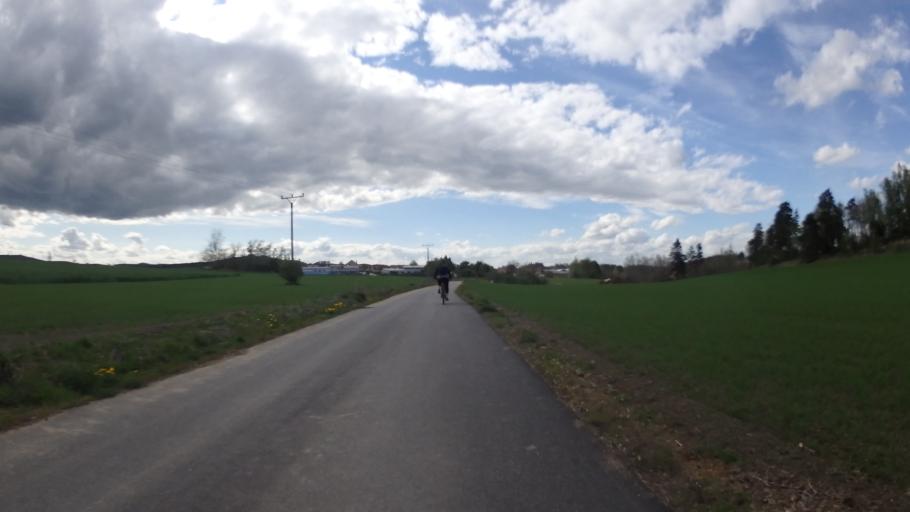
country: CZ
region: Vysocina
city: Merin
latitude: 49.3601
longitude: 15.9136
